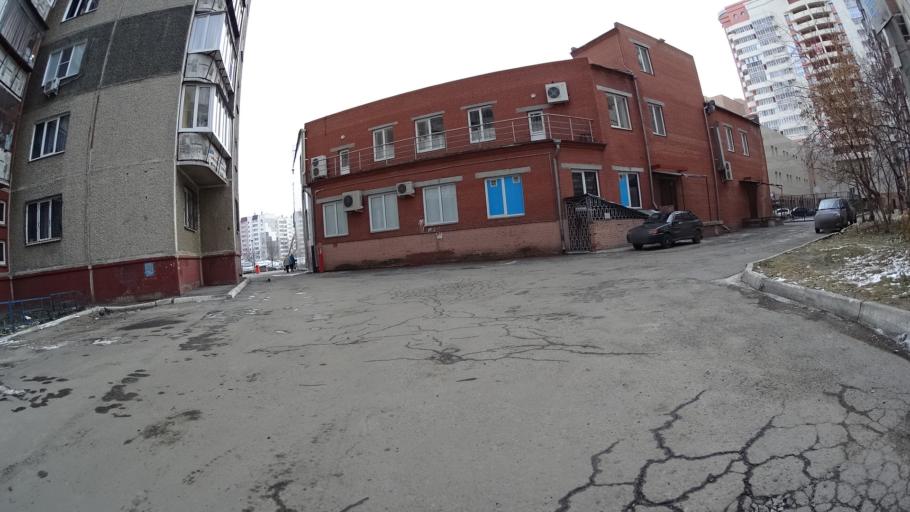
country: RU
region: Chelyabinsk
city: Roshchino
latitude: 55.1872
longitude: 61.3003
